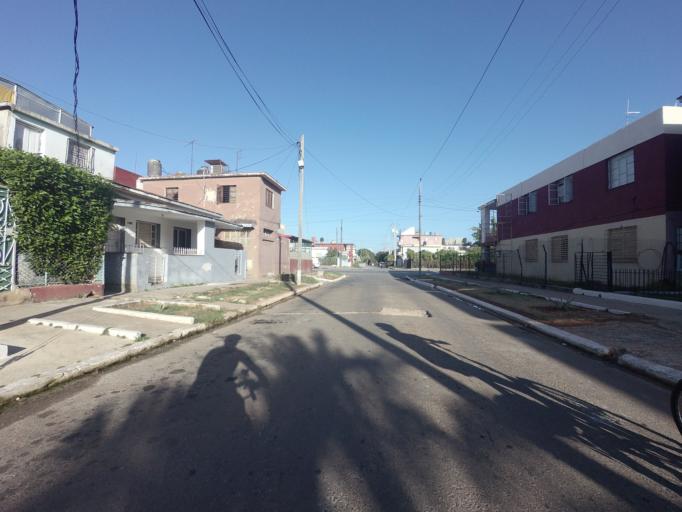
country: CU
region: La Habana
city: Cerro
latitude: 23.1011
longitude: -82.4306
